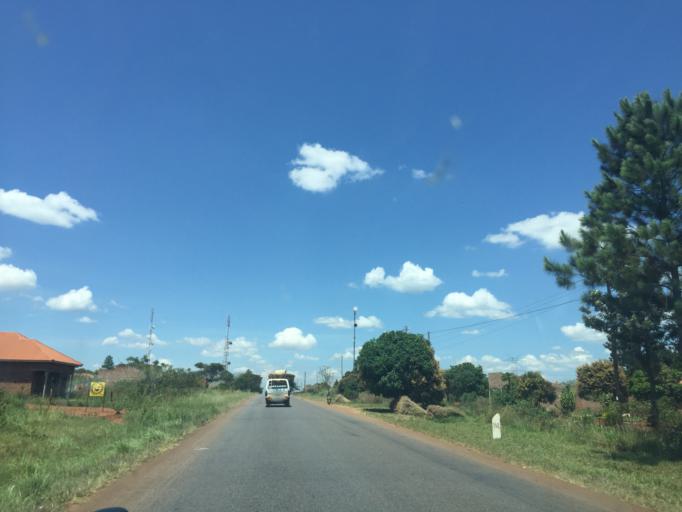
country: UG
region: Western Region
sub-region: Kiryandongo District
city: Masindi Port
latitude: 1.5061
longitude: 32.1028
